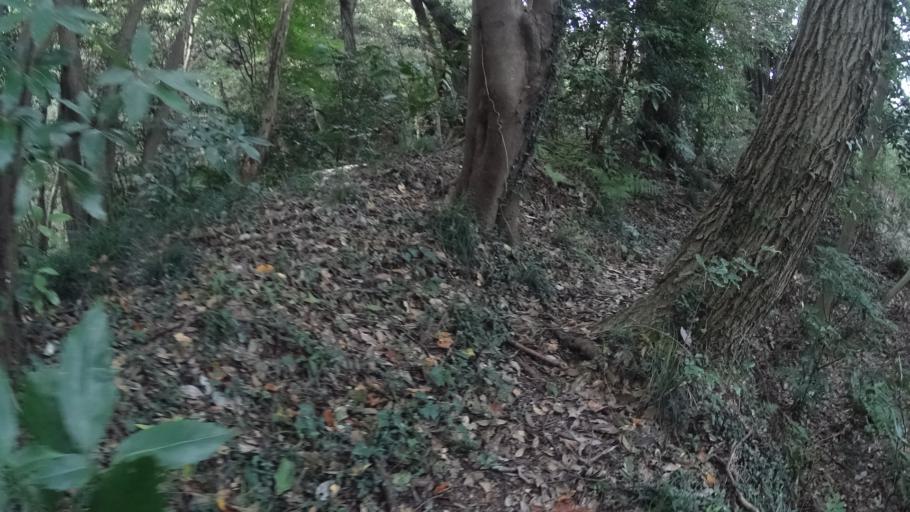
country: JP
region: Kanagawa
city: Kamakura
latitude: 35.3549
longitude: 139.5960
